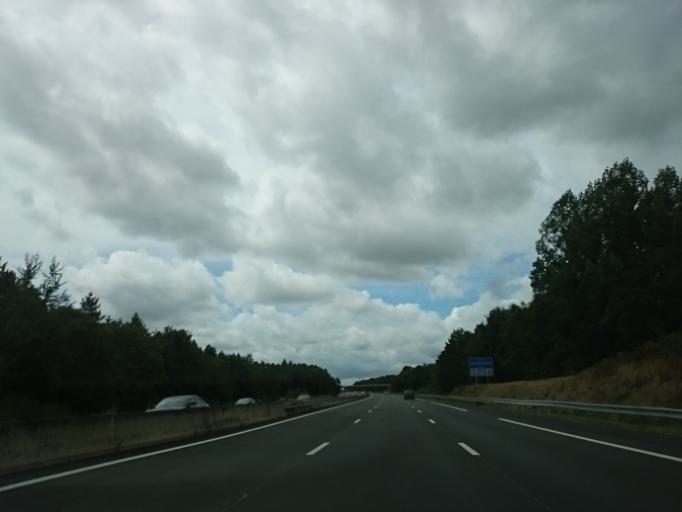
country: FR
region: Pays de la Loire
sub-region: Departement de la Sarthe
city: Montfort-le-Gesnois
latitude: 48.0621
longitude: 0.3919
